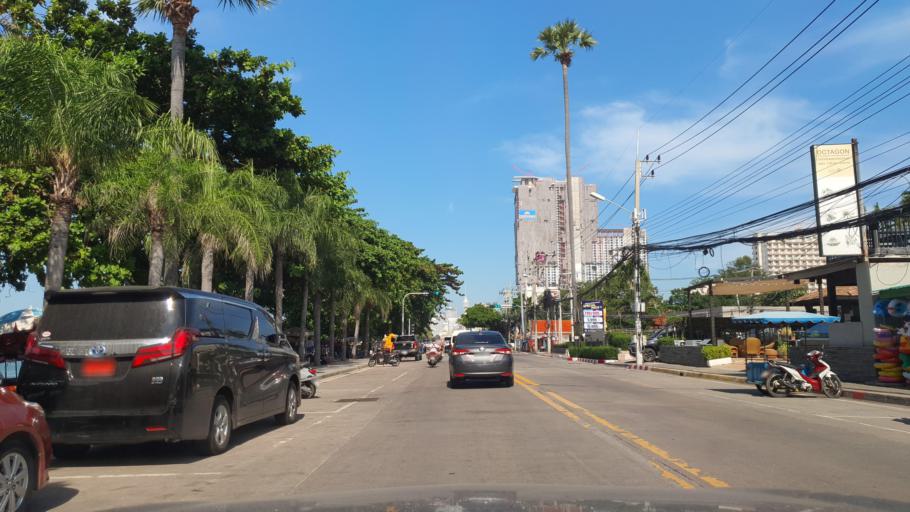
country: TH
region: Chon Buri
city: Phatthaya
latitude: 12.8853
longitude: 100.8788
